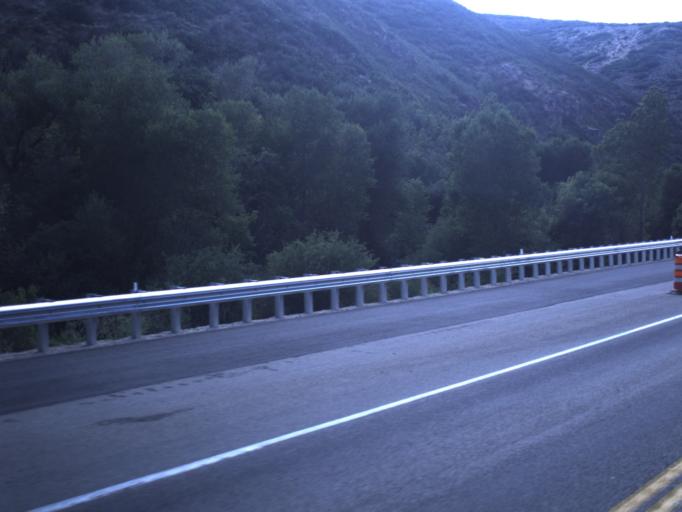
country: US
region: Utah
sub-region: Wasatch County
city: Heber
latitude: 40.4217
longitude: -111.3409
